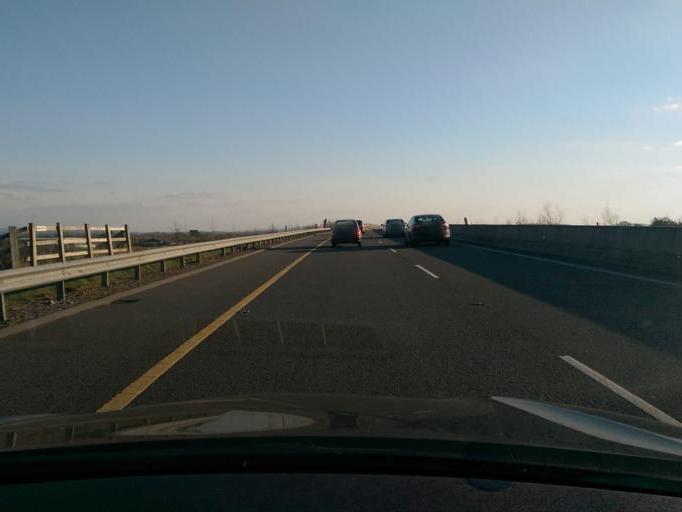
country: IE
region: Leinster
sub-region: Laois
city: Mountrath
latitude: 52.9812
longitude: -7.4325
